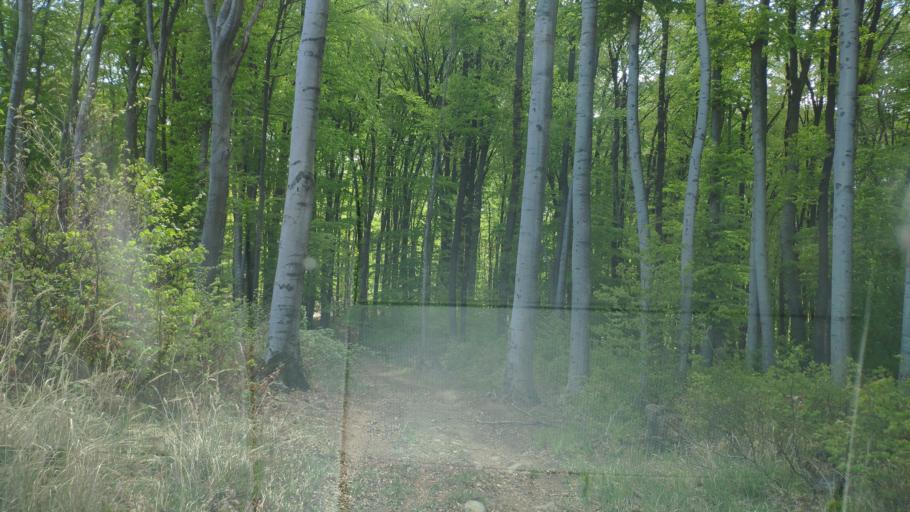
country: SK
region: Kosicky
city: Kosice
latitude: 48.6616
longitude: 21.4419
